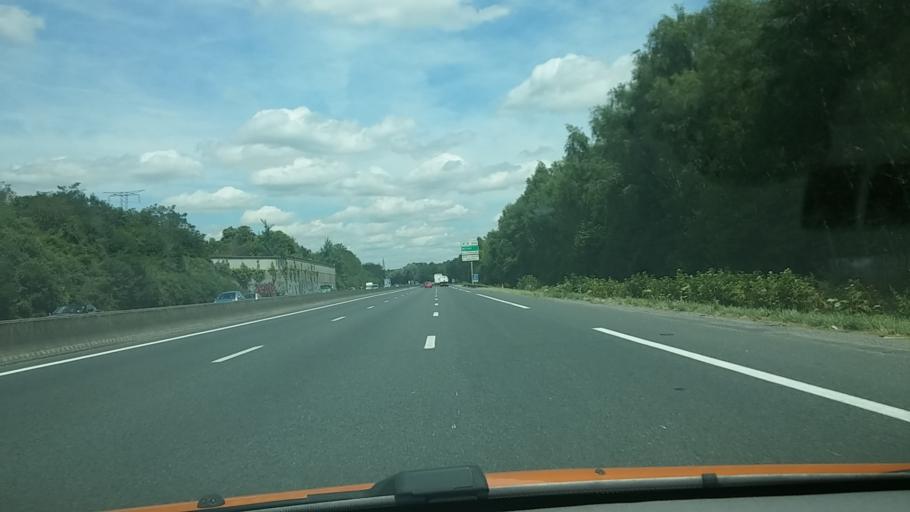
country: FR
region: Ile-de-France
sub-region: Departement de Seine-et-Marne
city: Pomponne
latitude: 48.8852
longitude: 2.6679
